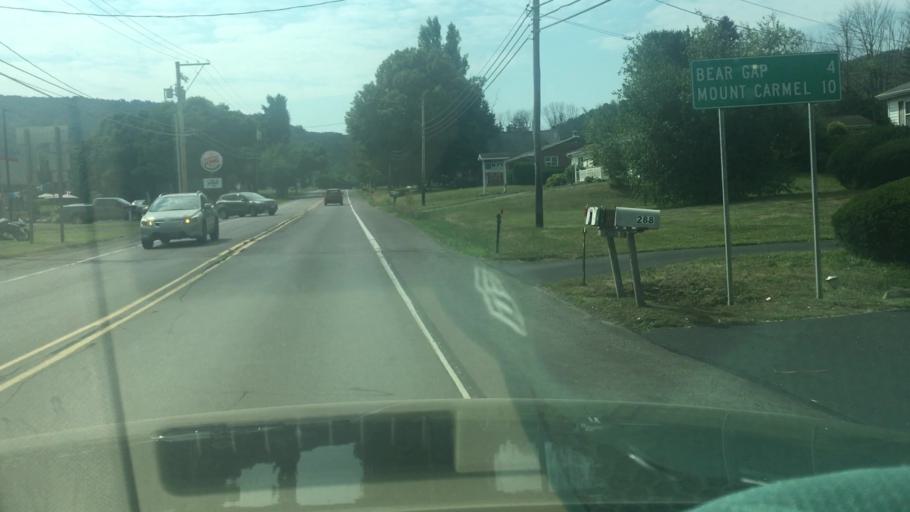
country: US
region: Pennsylvania
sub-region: Northumberland County
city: Elysburg
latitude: 40.8603
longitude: -76.5479
